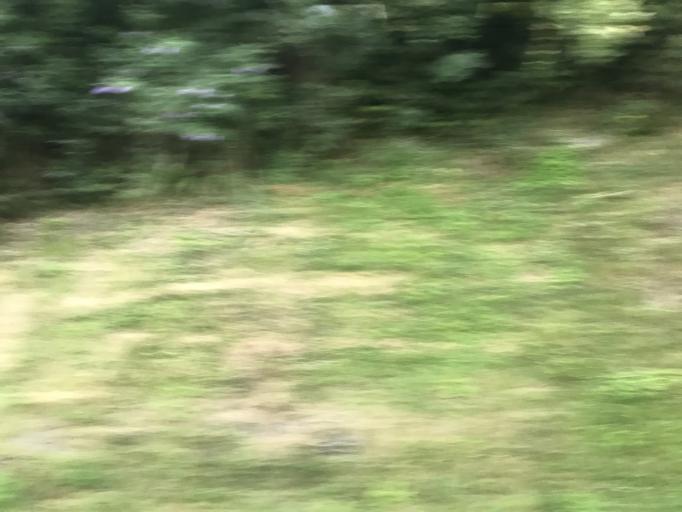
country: ES
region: Basque Country
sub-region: Provincia de Guipuzcoa
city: Icazteguieta
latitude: 43.0860
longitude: -2.1354
